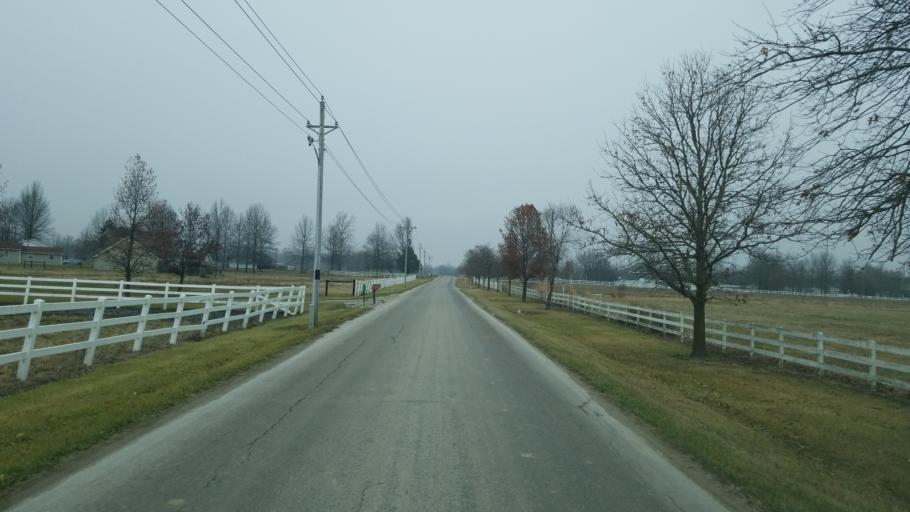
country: US
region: Indiana
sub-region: Adams County
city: Geneva
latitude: 40.5586
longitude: -84.9060
